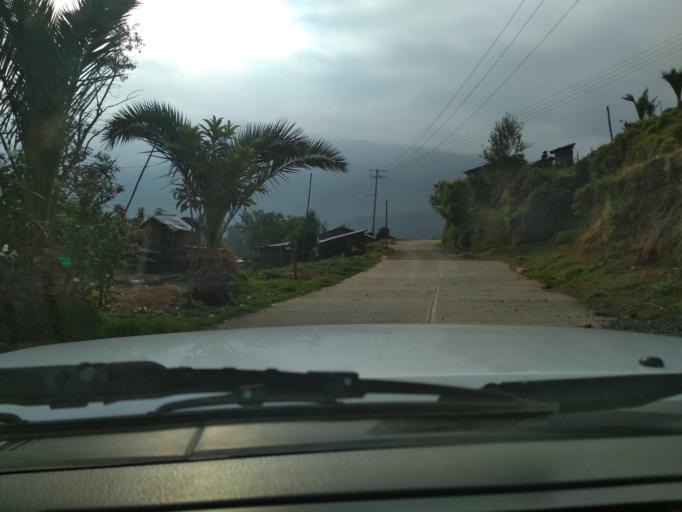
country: MX
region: Veracruz
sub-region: Soledad Atzompa
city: Tlatilpa
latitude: 18.7492
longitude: -97.1538
